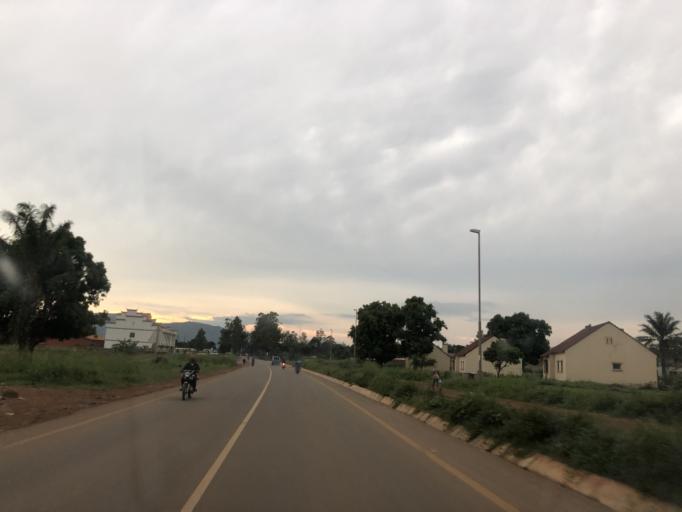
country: AO
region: Cuanza Sul
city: Uacu Cungo
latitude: -11.3517
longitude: 15.1131
